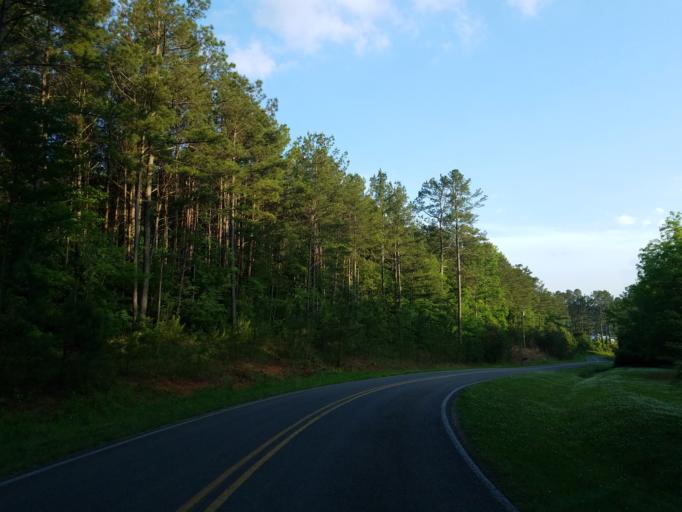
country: US
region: Georgia
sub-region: Cherokee County
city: Ball Ground
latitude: 34.3022
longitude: -84.3681
